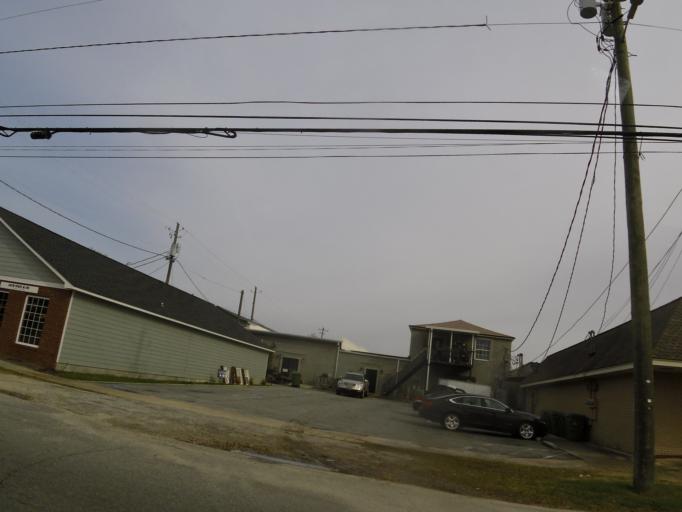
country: US
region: Georgia
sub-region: Seminole County
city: Donalsonville
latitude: 31.0409
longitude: -84.8825
